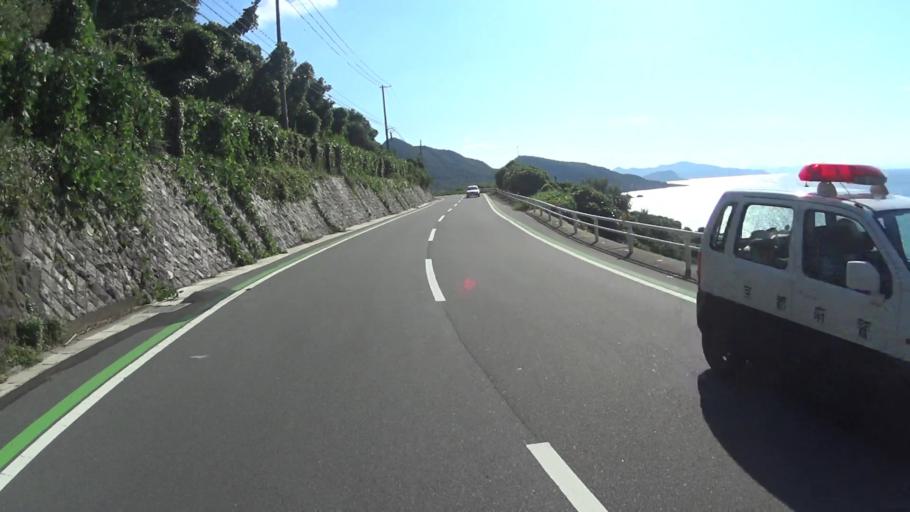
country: JP
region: Kyoto
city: Miyazu
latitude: 35.7278
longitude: 135.0870
